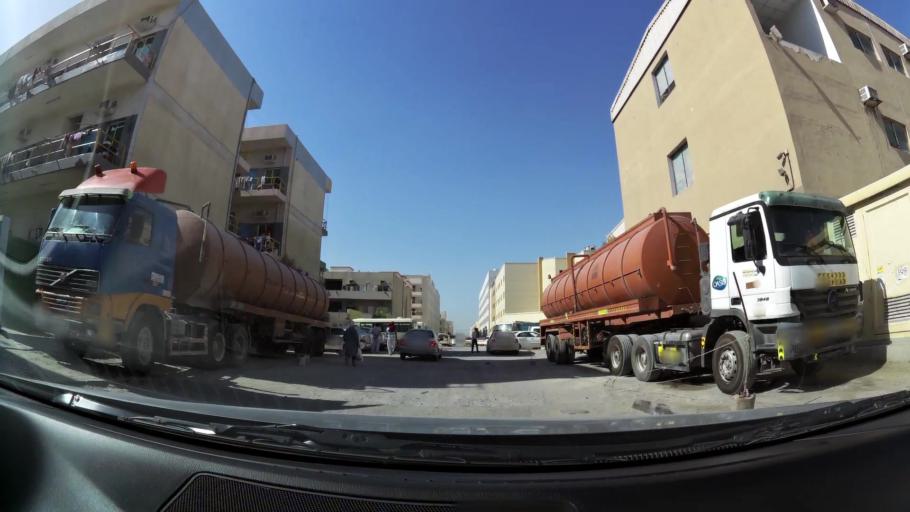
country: AE
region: Dubai
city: Dubai
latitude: 25.0060
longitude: 55.1081
